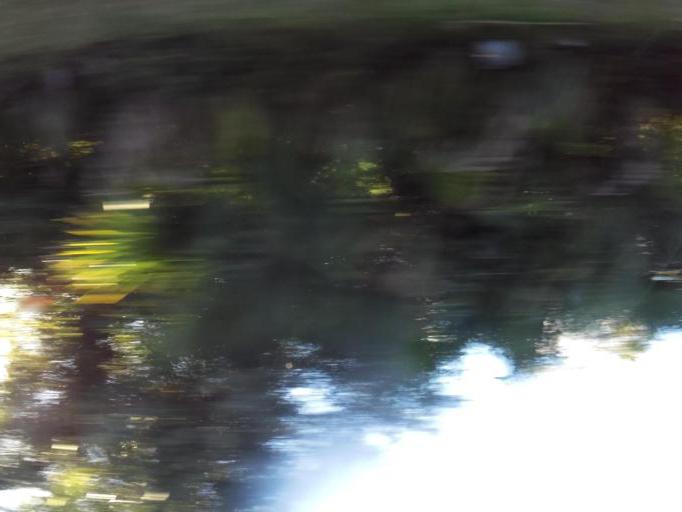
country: US
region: Florida
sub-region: Marion County
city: Citra
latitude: 29.4550
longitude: -82.1158
